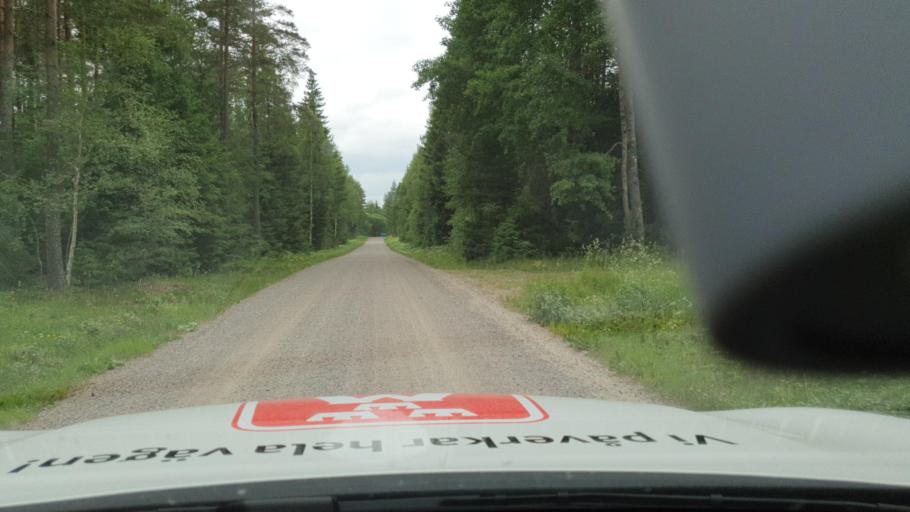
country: SE
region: Vaestra Goetaland
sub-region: Tidaholms Kommun
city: Tidaholm
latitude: 58.1607
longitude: 14.0445
